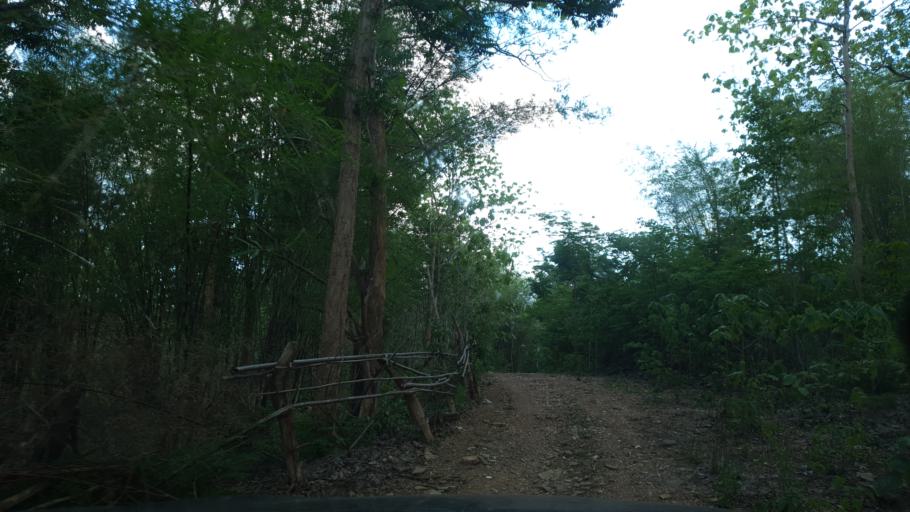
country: TH
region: Lampang
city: Sop Prap
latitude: 17.8907
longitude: 99.2871
